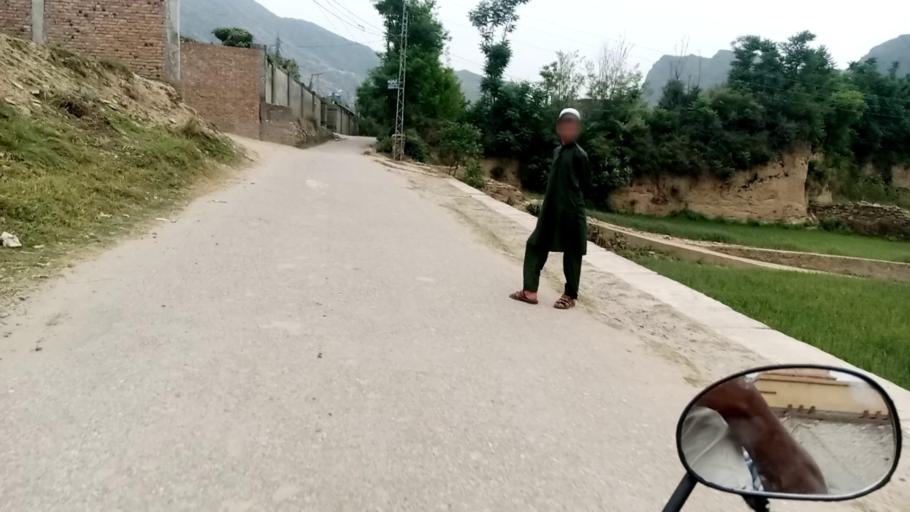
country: PK
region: Khyber Pakhtunkhwa
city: Saidu Sharif
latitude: 34.7562
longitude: 72.3786
